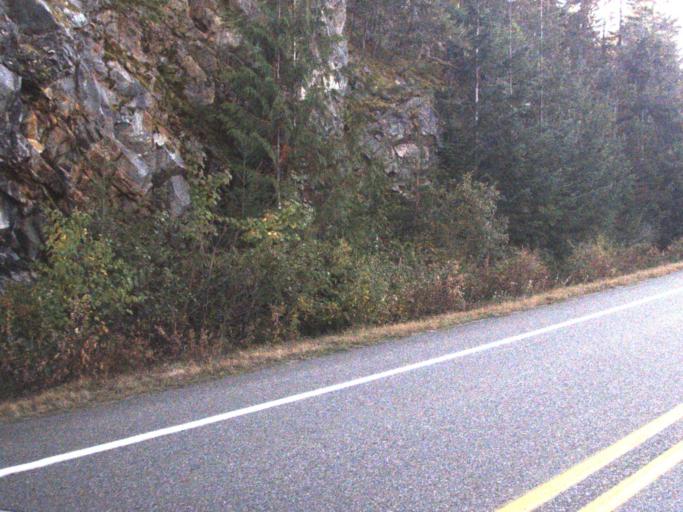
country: US
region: Washington
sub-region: Snohomish County
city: Darrington
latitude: 48.7282
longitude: -121.0419
